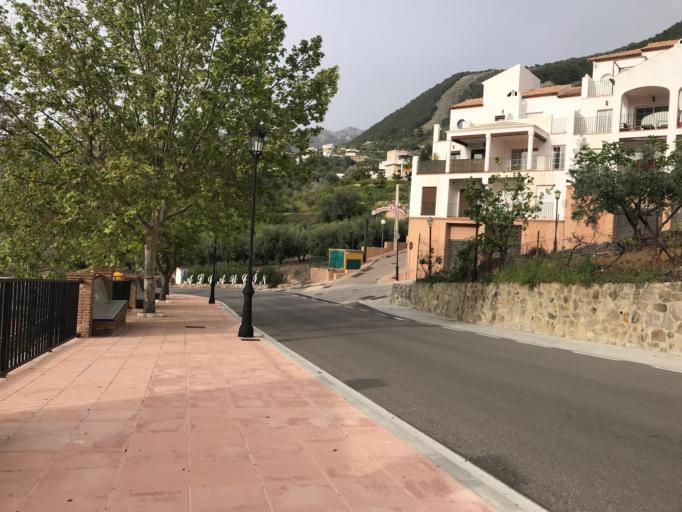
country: ES
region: Andalusia
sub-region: Provincia de Malaga
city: Alcaucin
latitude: 36.9043
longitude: -4.1159
